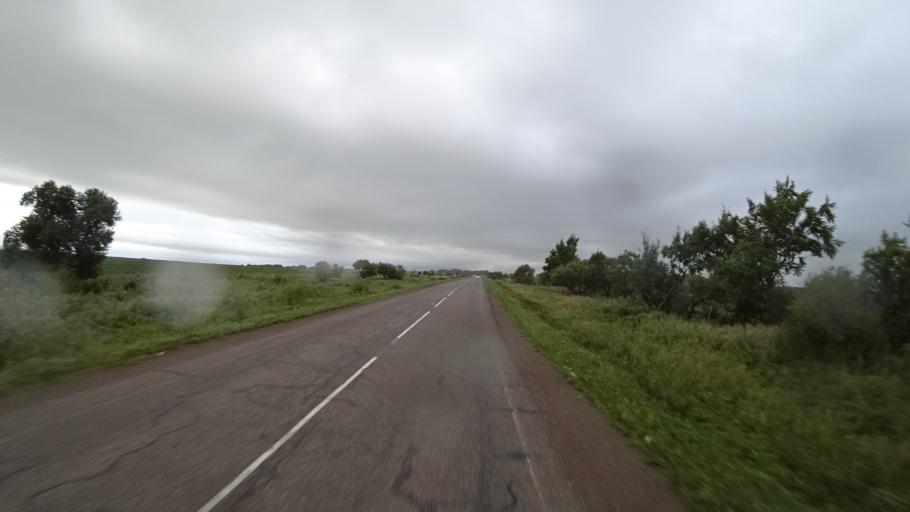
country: RU
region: Primorskiy
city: Chernigovka
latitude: 44.3638
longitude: 132.5452
